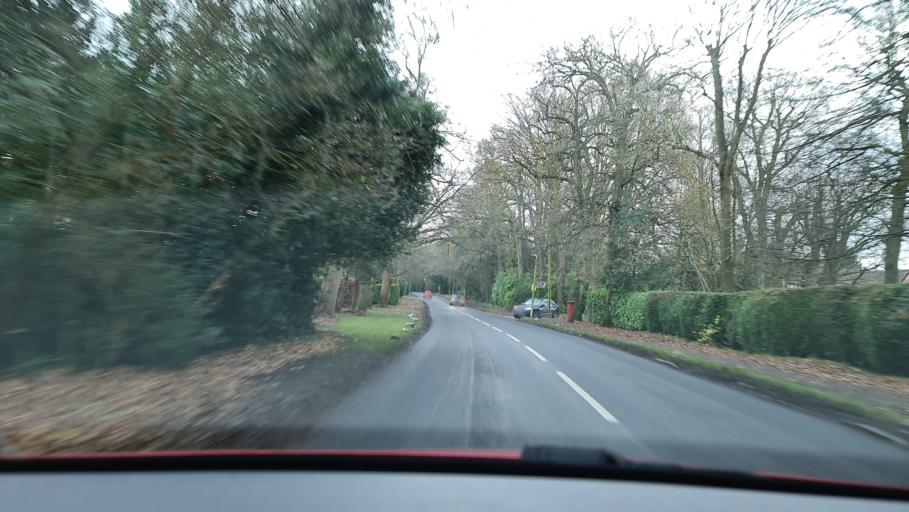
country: GB
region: England
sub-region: Buckinghamshire
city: Amersham on the Hill
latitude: 51.6853
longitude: -0.6211
